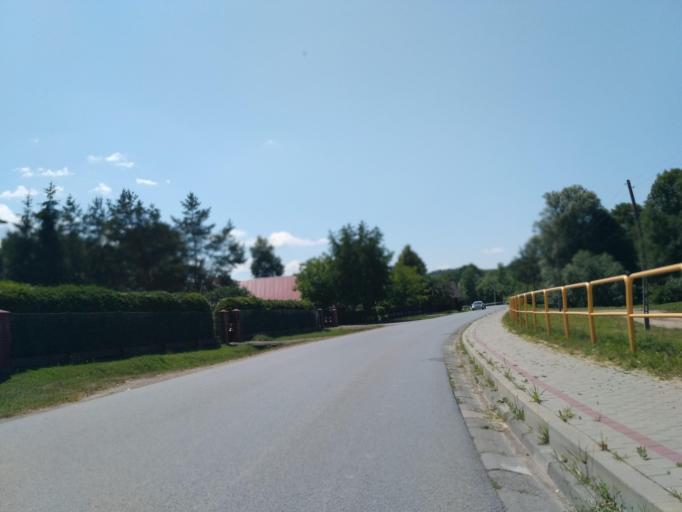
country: PL
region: Subcarpathian Voivodeship
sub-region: Powiat sanocki
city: Niebieszczany
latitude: 49.5257
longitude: 22.1279
